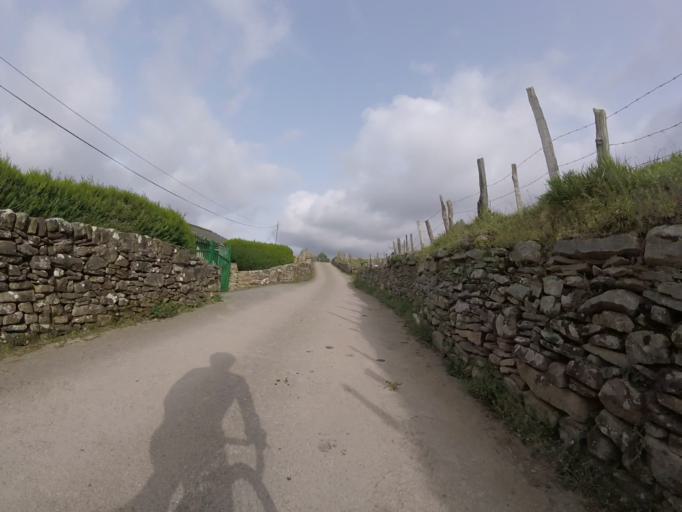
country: ES
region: Basque Country
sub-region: Provincia de Guipuzcoa
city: Berastegui
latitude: 43.1120
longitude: -1.9622
